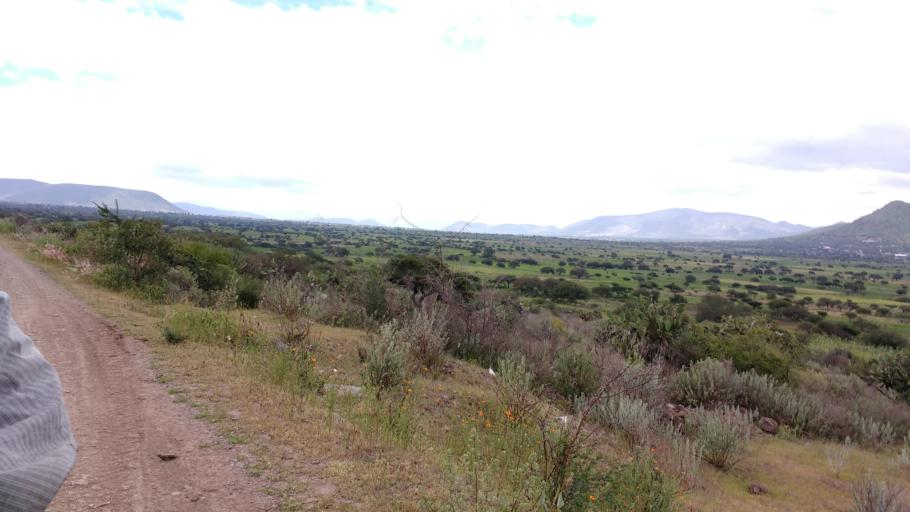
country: MX
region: Hidalgo
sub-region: Tezontepec de Aldama
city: Tenango
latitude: 20.2349
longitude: -99.2736
